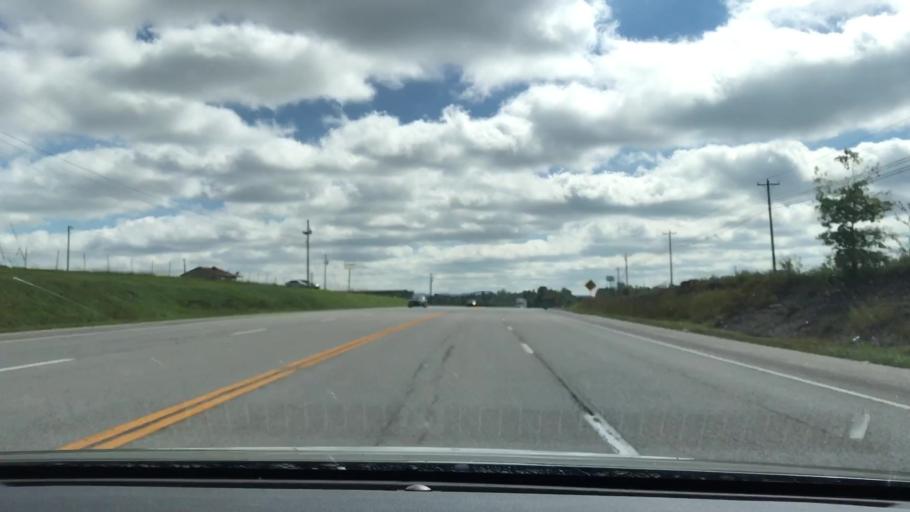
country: US
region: Kentucky
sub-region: McCreary County
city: Pine Knot
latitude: 36.6444
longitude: -84.4337
